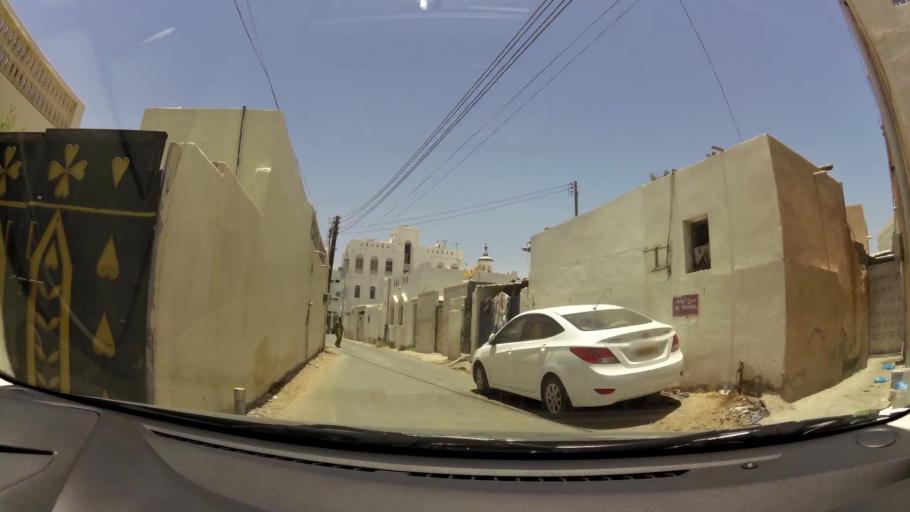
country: OM
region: Muhafazat Masqat
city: As Sib al Jadidah
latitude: 23.6367
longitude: 58.2297
